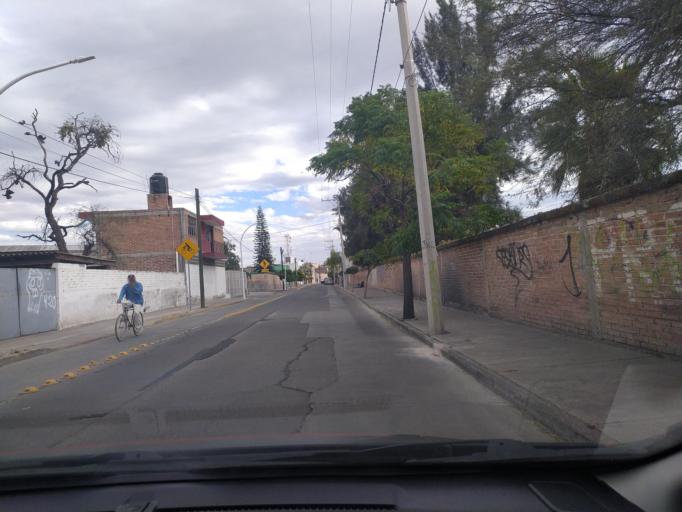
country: LA
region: Oudomxai
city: Muang La
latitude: 21.0203
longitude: 101.8628
